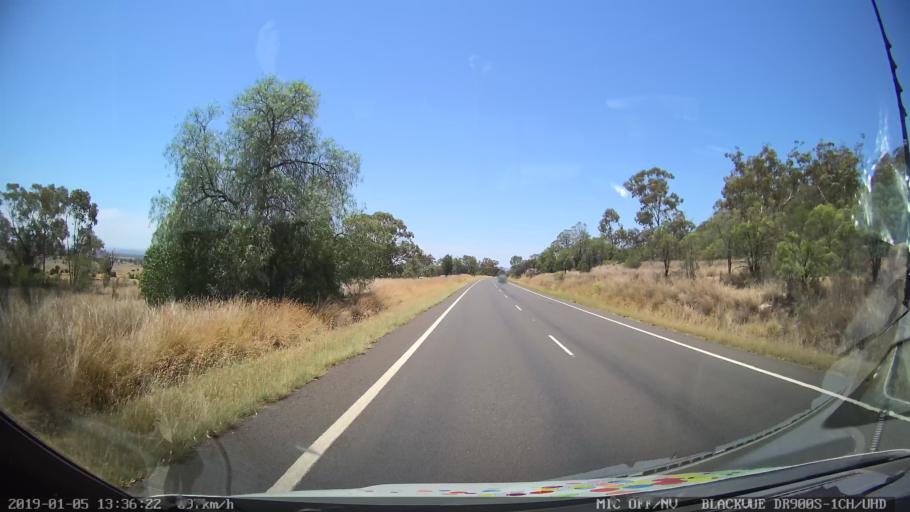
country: AU
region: New South Wales
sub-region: Gunnedah
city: Gunnedah
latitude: -30.9854
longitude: 150.1635
